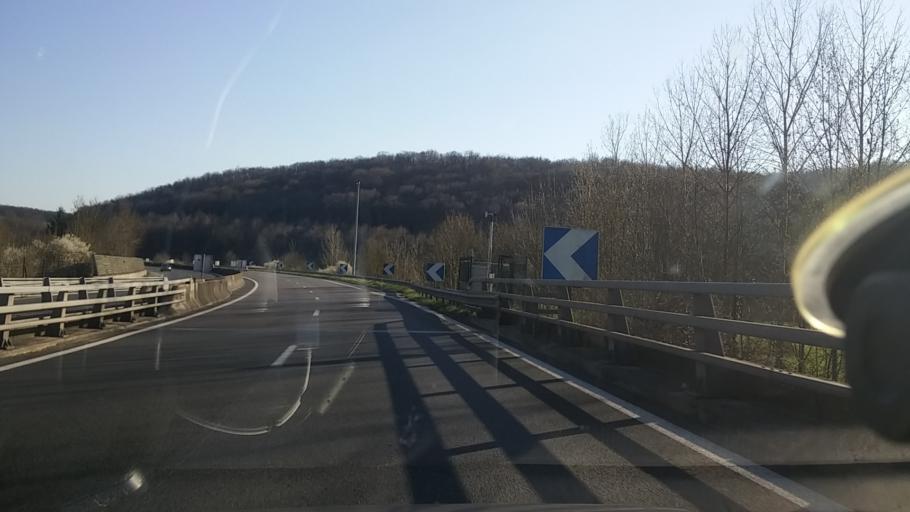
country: FR
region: Centre
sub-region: Departement de l'Indre
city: Saint-Marcel
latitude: 46.6023
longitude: 1.4989
